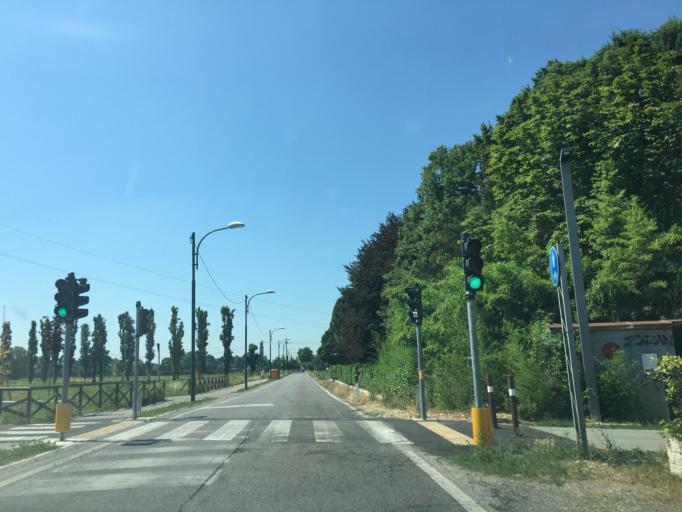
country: IT
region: Veneto
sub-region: Provincia di Venezia
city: Zelarino
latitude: 45.4926
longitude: 12.1911
